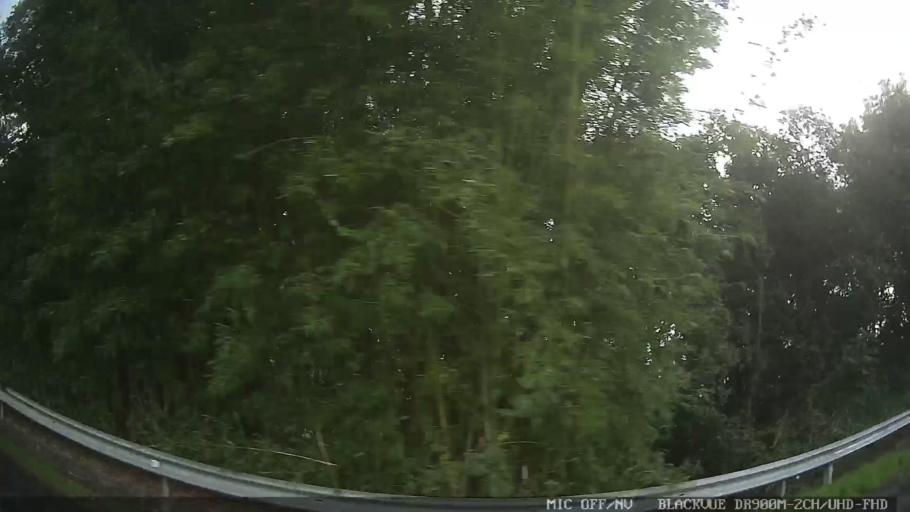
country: BR
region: Sao Paulo
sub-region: Porto Feliz
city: Porto Feliz
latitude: -23.1991
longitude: -47.6089
